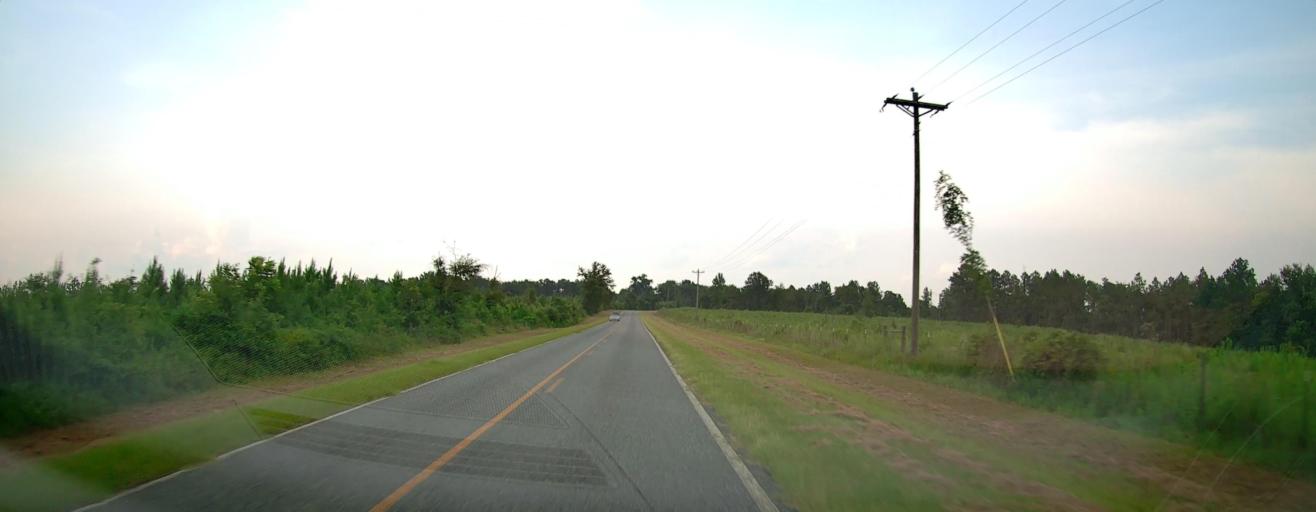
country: US
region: Georgia
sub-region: Laurens County
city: East Dublin
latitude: 32.6426
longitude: -82.8286
